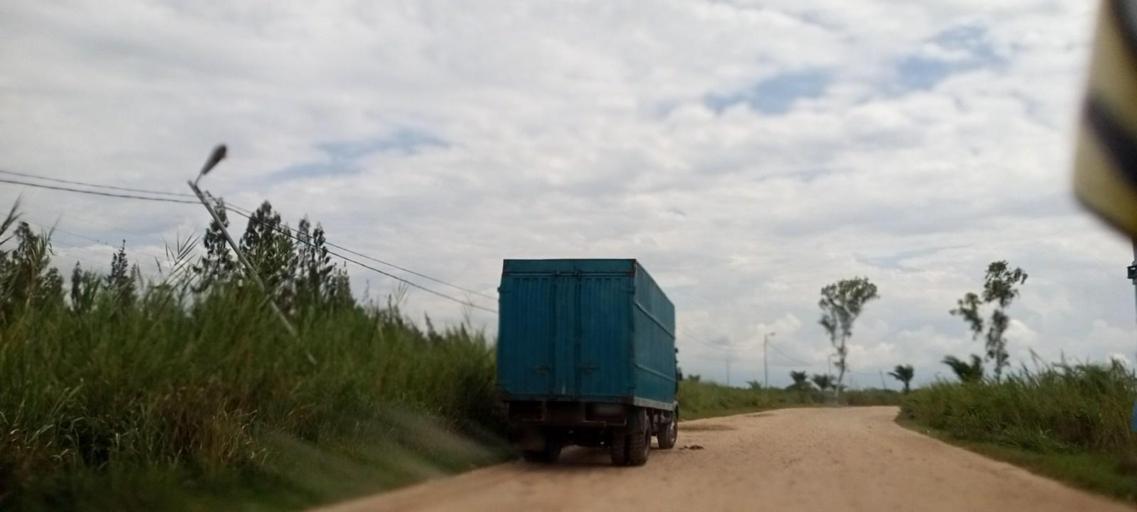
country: CD
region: South Kivu
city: Uvira
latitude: -3.3394
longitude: 29.2037
